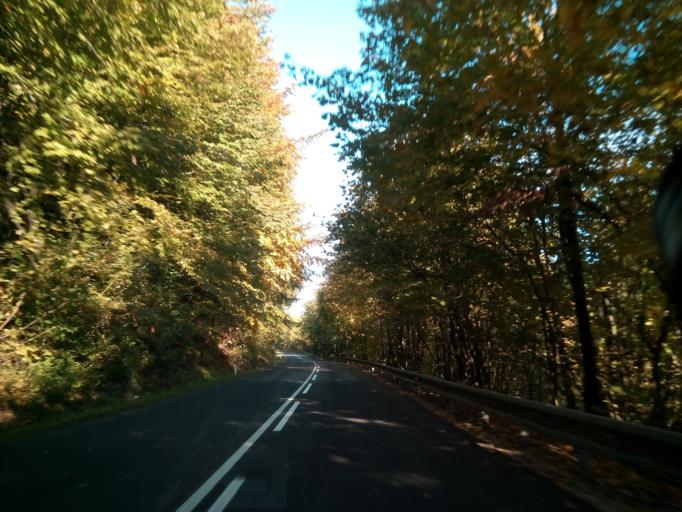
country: SK
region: Kosicky
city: Gelnica
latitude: 48.8351
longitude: 21.0551
